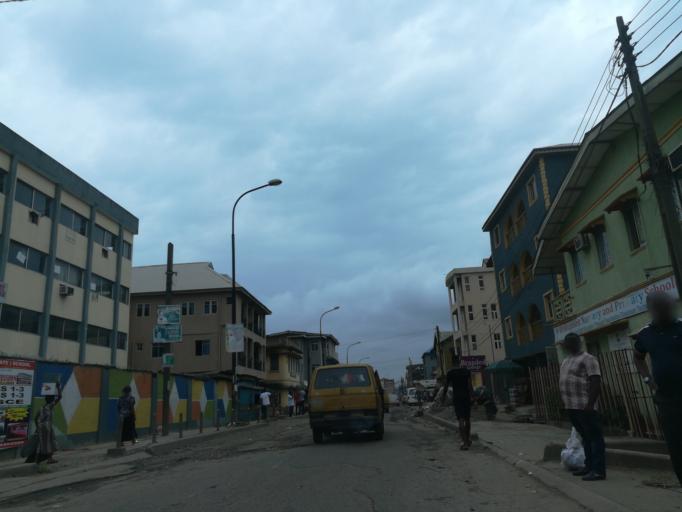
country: NG
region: Lagos
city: Ebute Metta
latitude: 6.4863
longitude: 3.3843
